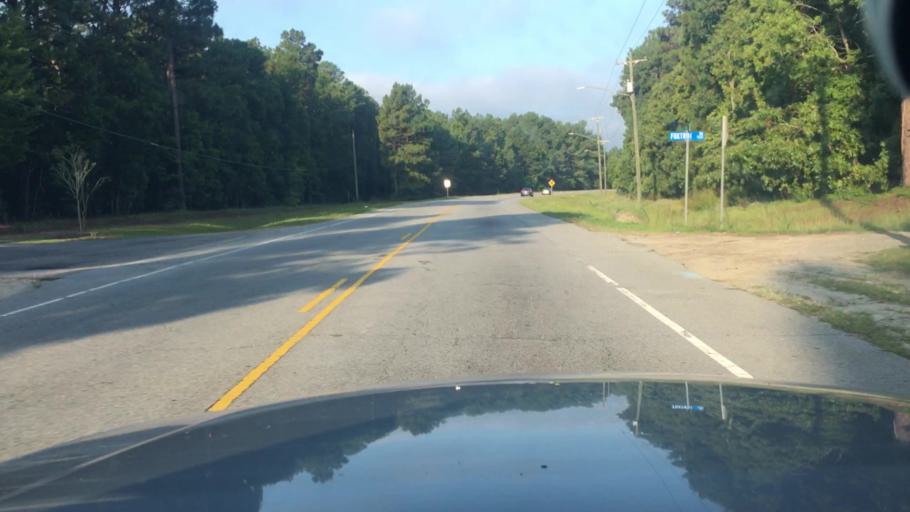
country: US
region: North Carolina
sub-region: Cumberland County
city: Fort Bragg
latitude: 35.1047
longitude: -78.9487
